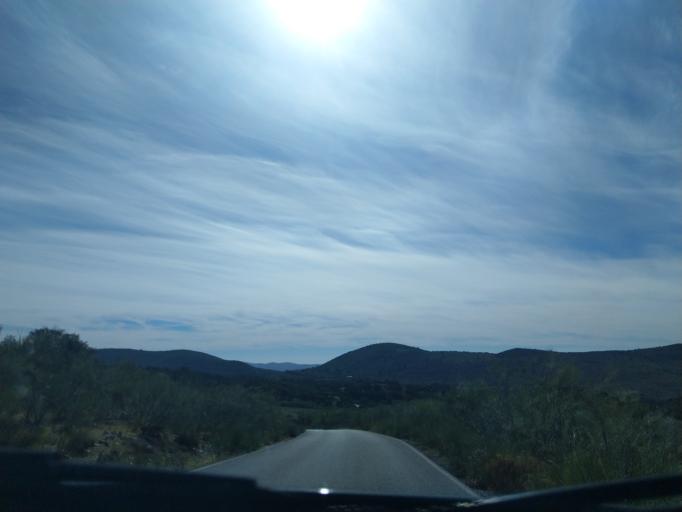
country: ES
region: Extremadura
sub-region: Provincia de Badajoz
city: Reina
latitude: 38.1429
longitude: -5.9161
